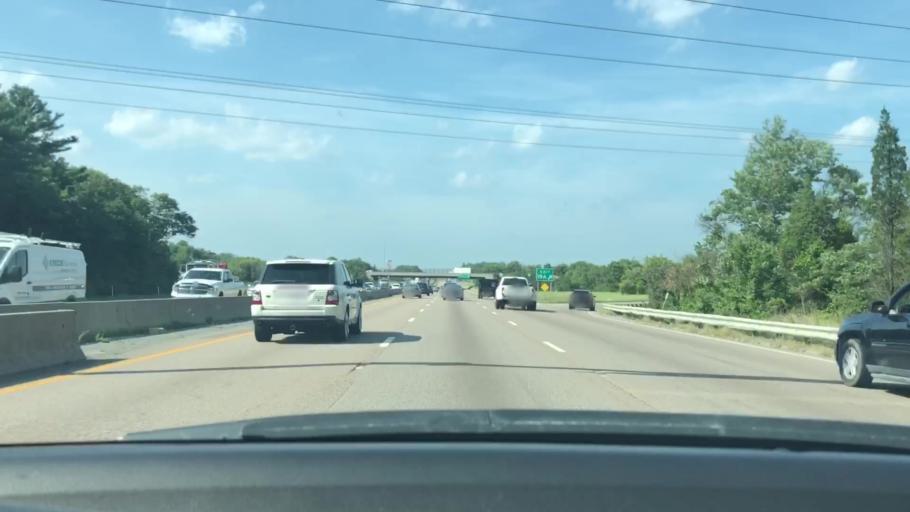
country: US
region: Massachusetts
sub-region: Norfolk County
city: Avon
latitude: 42.1218
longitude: -71.0615
